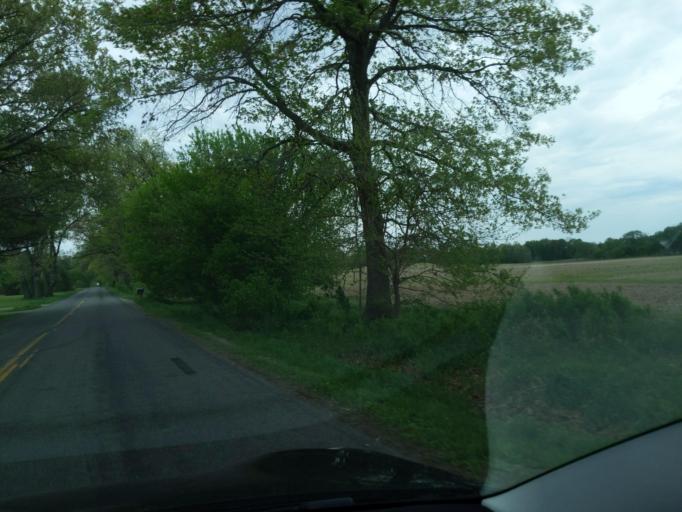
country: US
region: Michigan
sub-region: Ingham County
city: Stockbridge
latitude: 42.4437
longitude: -84.2146
